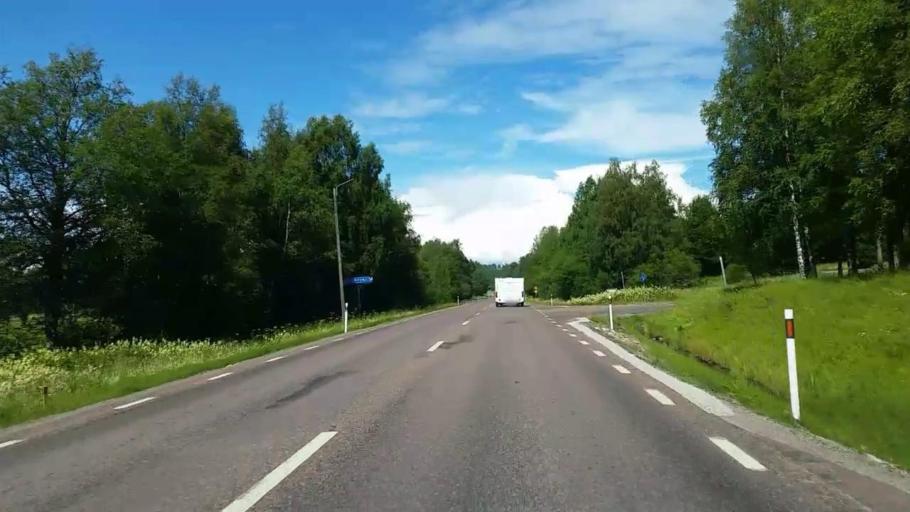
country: SE
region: Dalarna
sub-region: Rattviks Kommun
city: Raettvik
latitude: 60.9841
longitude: 15.2222
